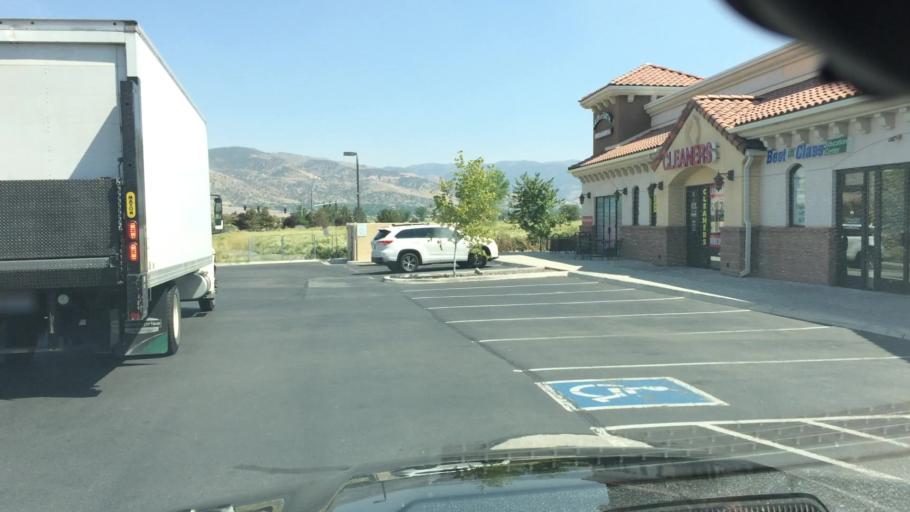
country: US
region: Nevada
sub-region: Washoe County
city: Sparks
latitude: 39.4253
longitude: -119.7506
